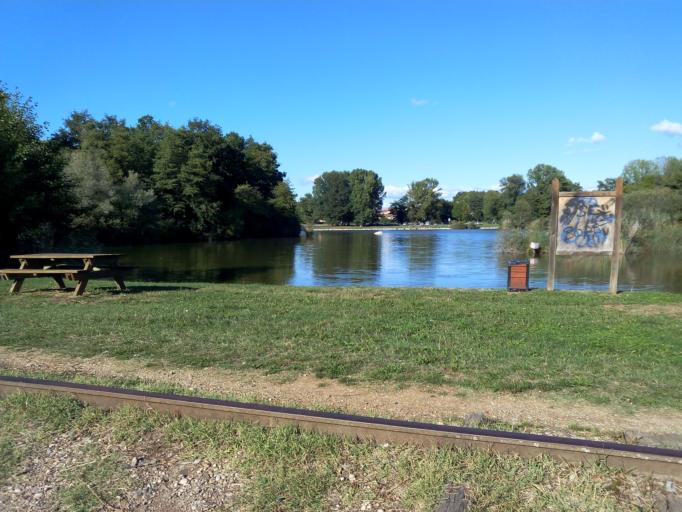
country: FR
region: Rhone-Alpes
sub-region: Departement de l'Isere
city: Charvieu-Chavagneux
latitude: 45.7500
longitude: 5.1520
